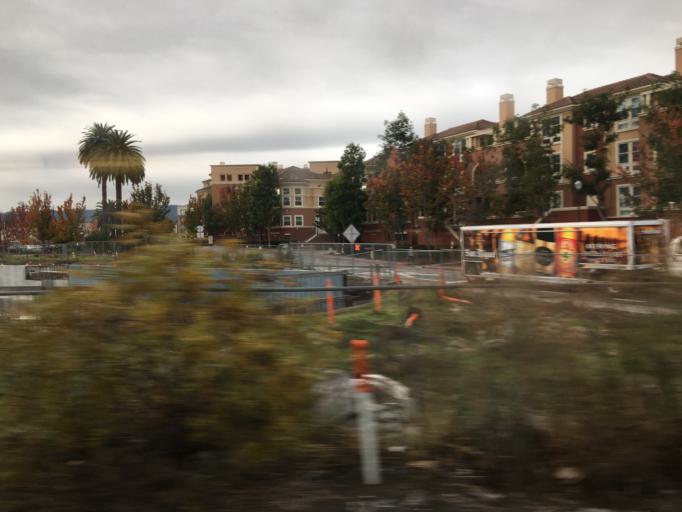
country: US
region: California
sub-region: San Mateo County
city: Redwood City
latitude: 37.4826
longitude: -122.2263
